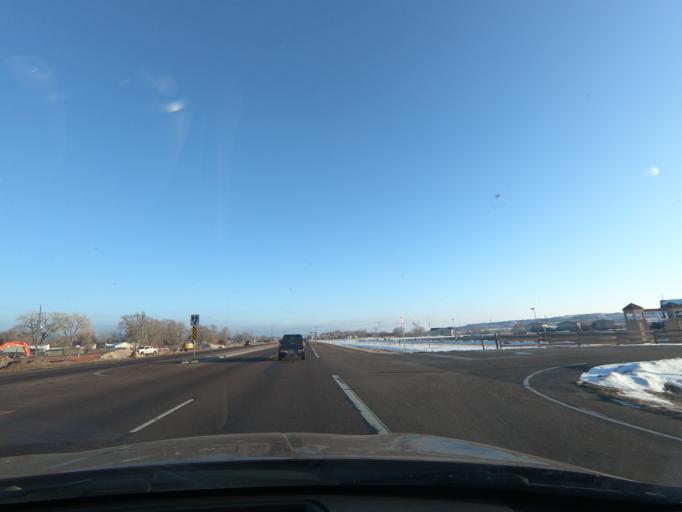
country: US
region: Colorado
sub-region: El Paso County
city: Security-Widefield
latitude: 38.7547
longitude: -104.7476
